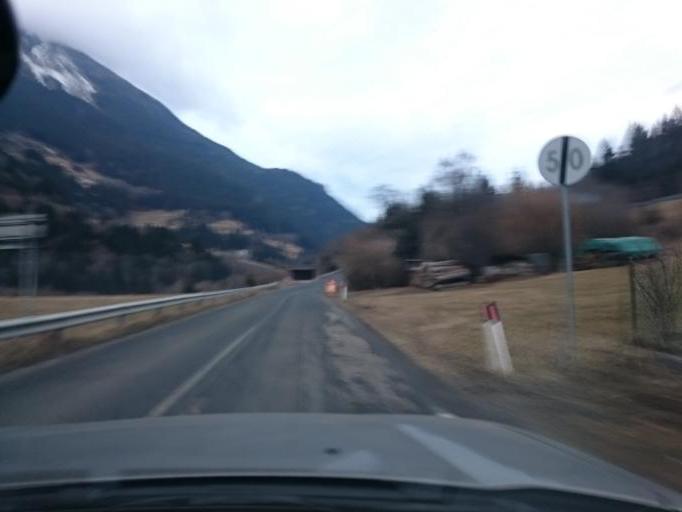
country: IT
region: Lombardy
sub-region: Provincia di Sondrio
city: Valdisotto
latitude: 46.4055
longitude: 10.3513
